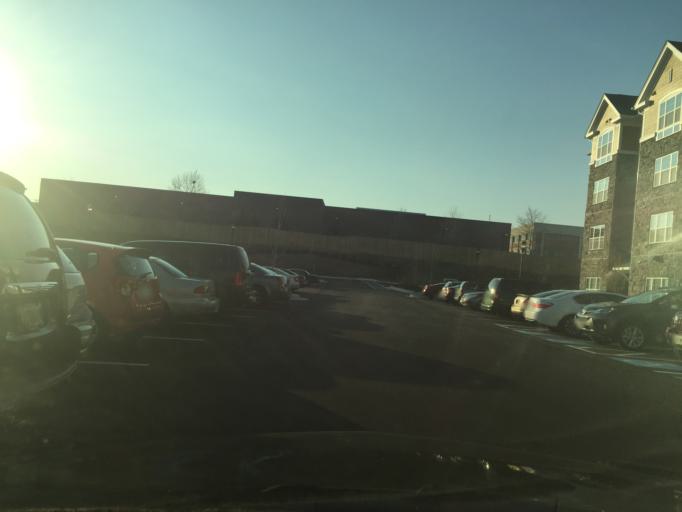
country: US
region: Maryland
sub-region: Baltimore County
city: Perry Hall
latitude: 39.4128
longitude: -76.4592
